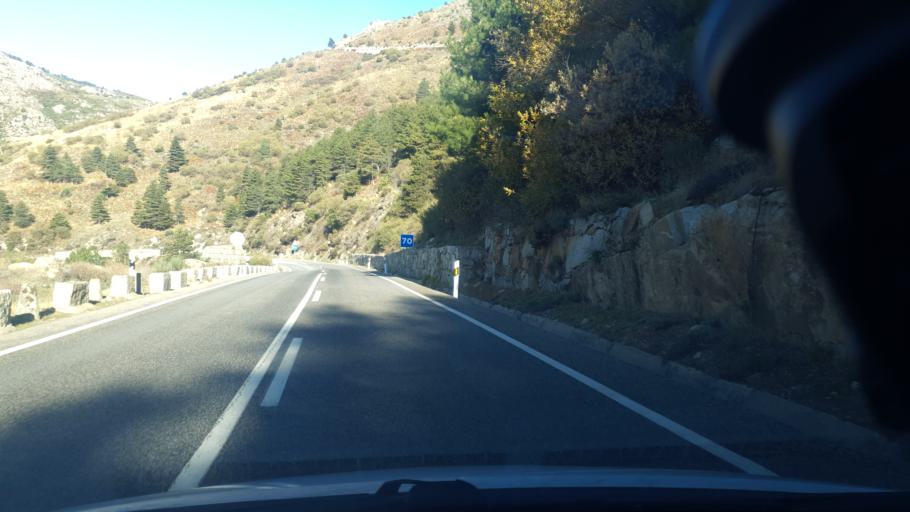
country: ES
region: Castille and Leon
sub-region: Provincia de Avila
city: Cuevas del Valle
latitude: 40.3119
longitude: -5.0069
